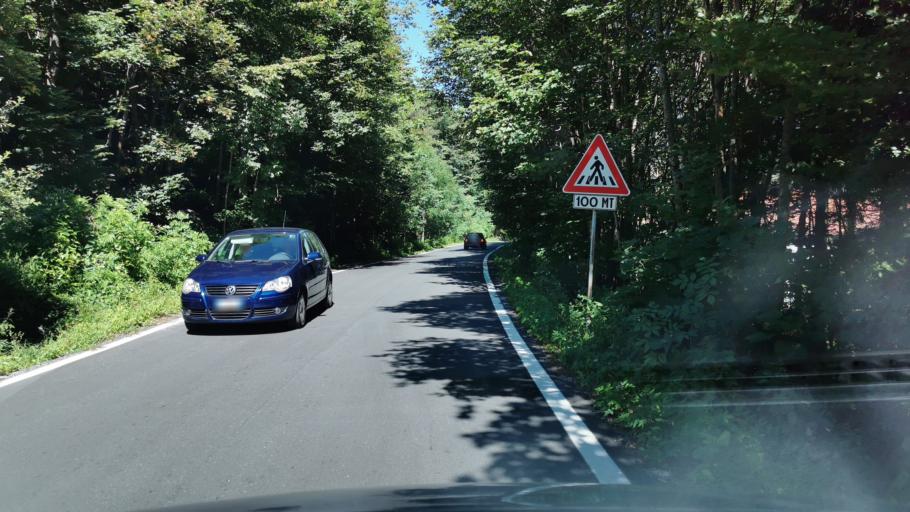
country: IT
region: Piedmont
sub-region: Provincia di Cuneo
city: Demonte
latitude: 44.2235
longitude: 7.2935
